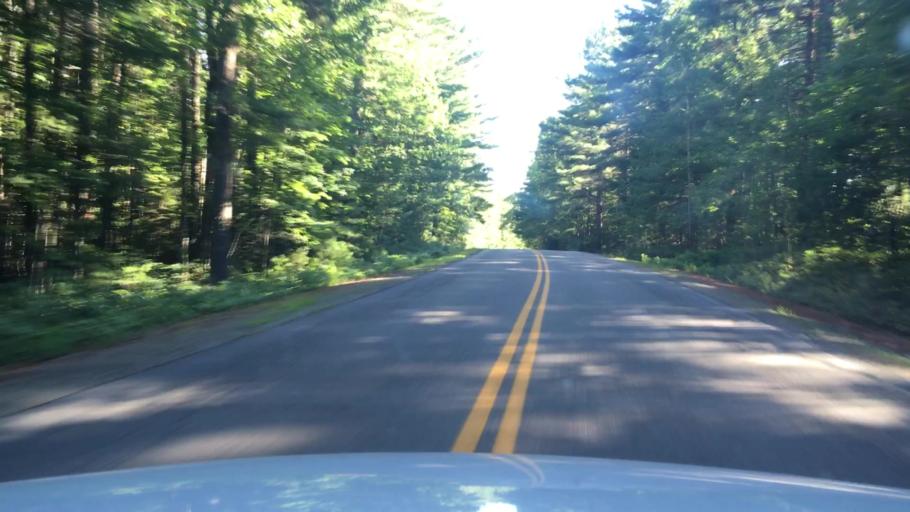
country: US
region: Maine
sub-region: Penobscot County
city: Enfield
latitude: 45.1935
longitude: -68.6063
